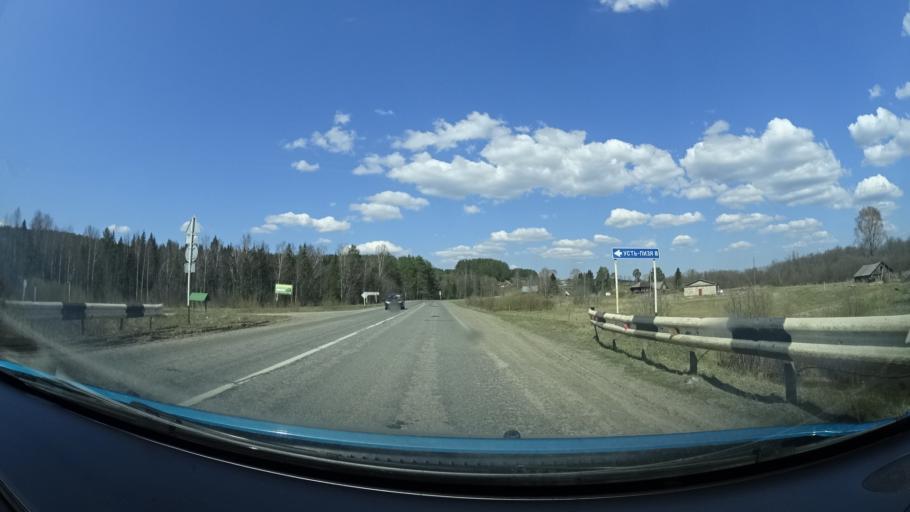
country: RU
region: Perm
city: Yugo-Kamskiy
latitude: 57.5446
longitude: 55.6846
